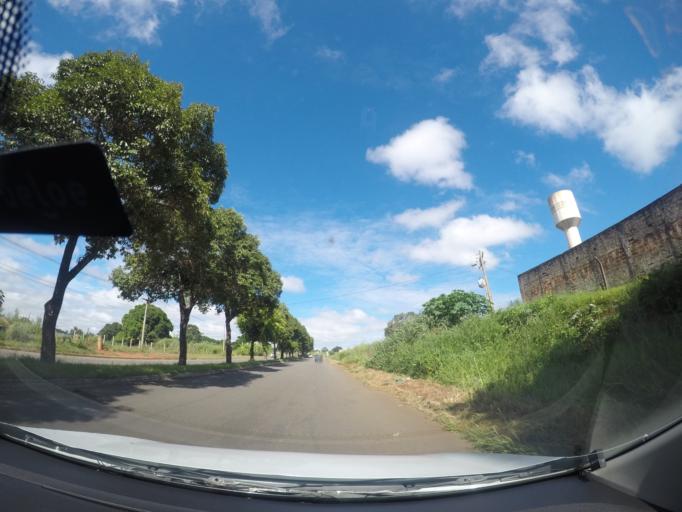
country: BR
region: Goias
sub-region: Goiania
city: Goiania
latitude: -16.6516
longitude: -49.1699
